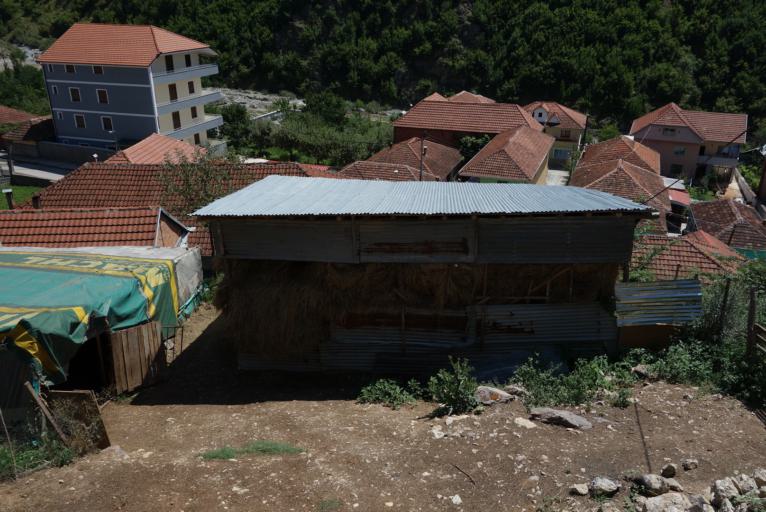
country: AL
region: Diber
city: Peshkopi
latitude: 41.6861
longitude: 20.4455
